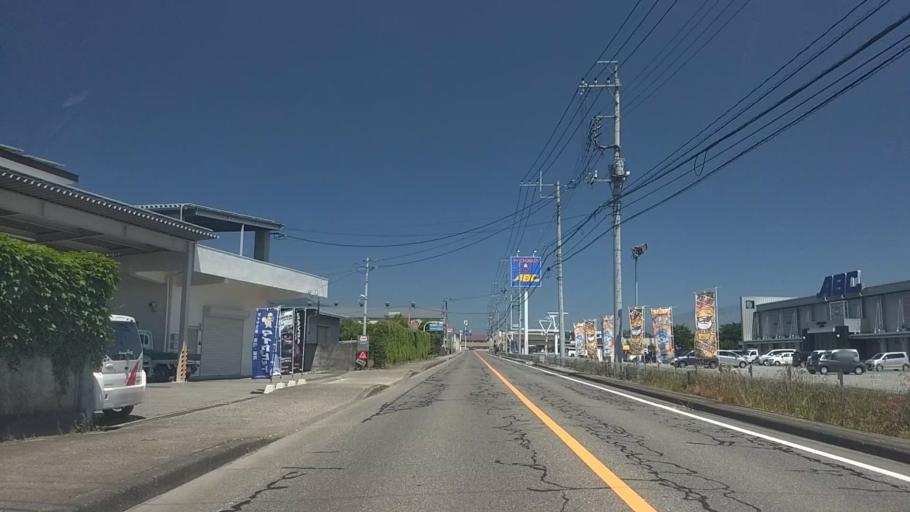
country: JP
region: Yamanashi
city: Nirasaki
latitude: 35.6935
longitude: 138.4586
